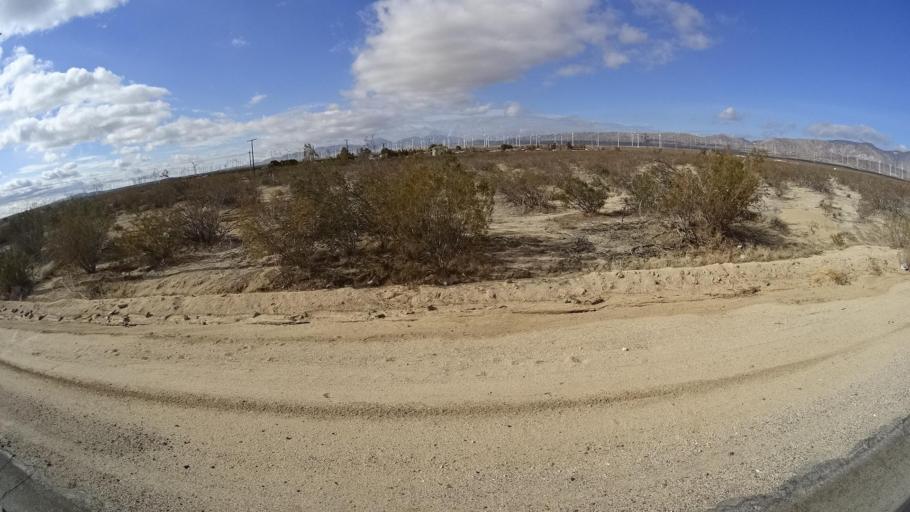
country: US
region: California
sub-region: Kern County
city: Mojave
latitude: 35.0615
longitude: -118.1858
